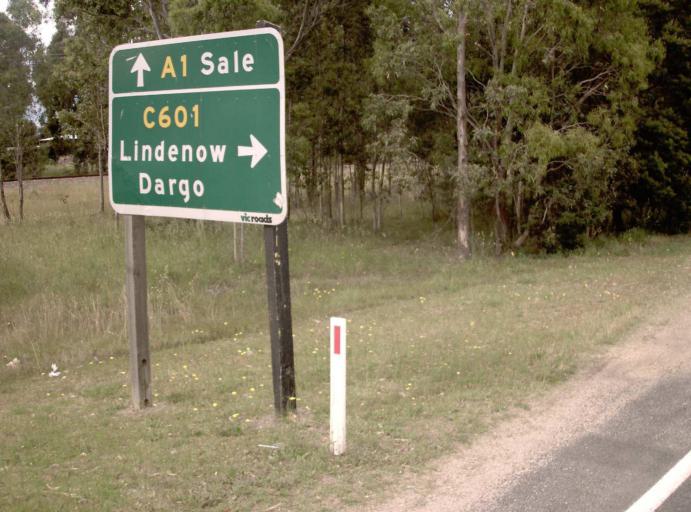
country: AU
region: Victoria
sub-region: East Gippsland
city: Bairnsdale
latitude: -37.8425
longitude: 147.5907
